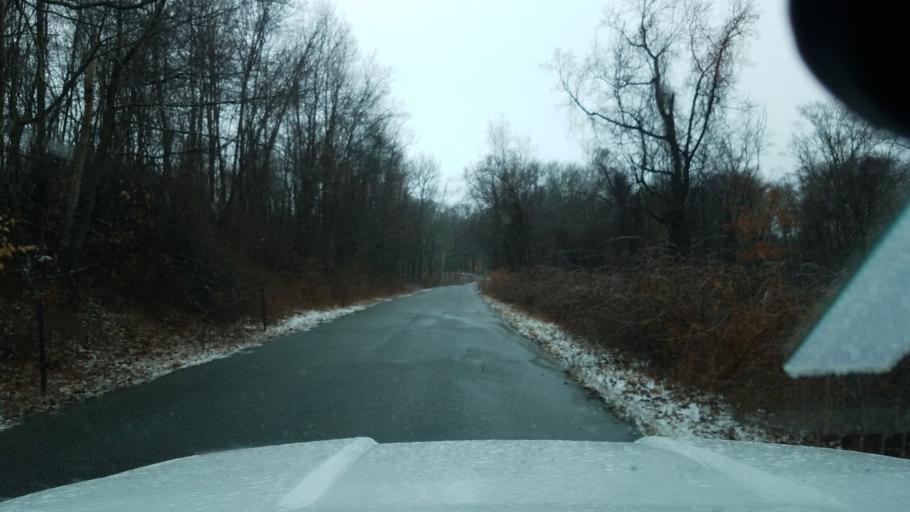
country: US
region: Connecticut
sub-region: New Haven County
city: Heritage Village
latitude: 41.4965
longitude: -73.2700
